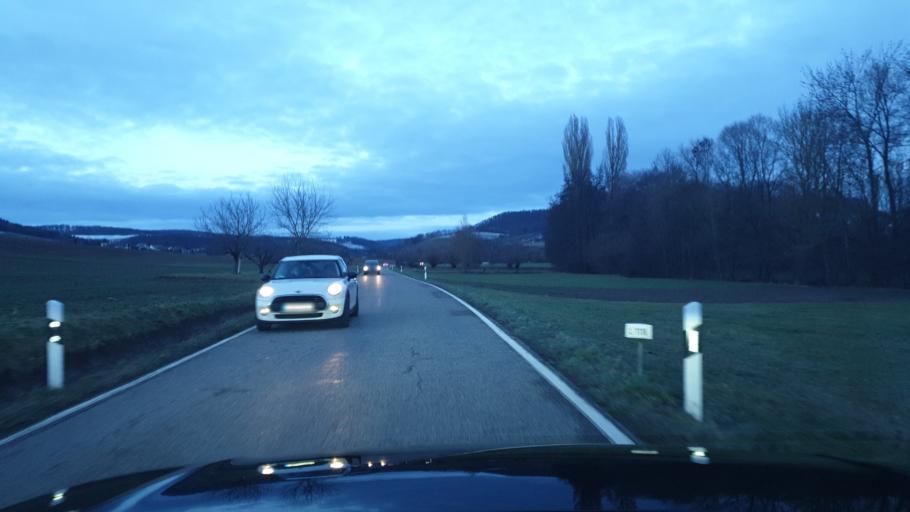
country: DE
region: Baden-Wuerttemberg
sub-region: Regierungsbezirk Stuttgart
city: Oberstenfeld
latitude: 49.0315
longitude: 9.3280
